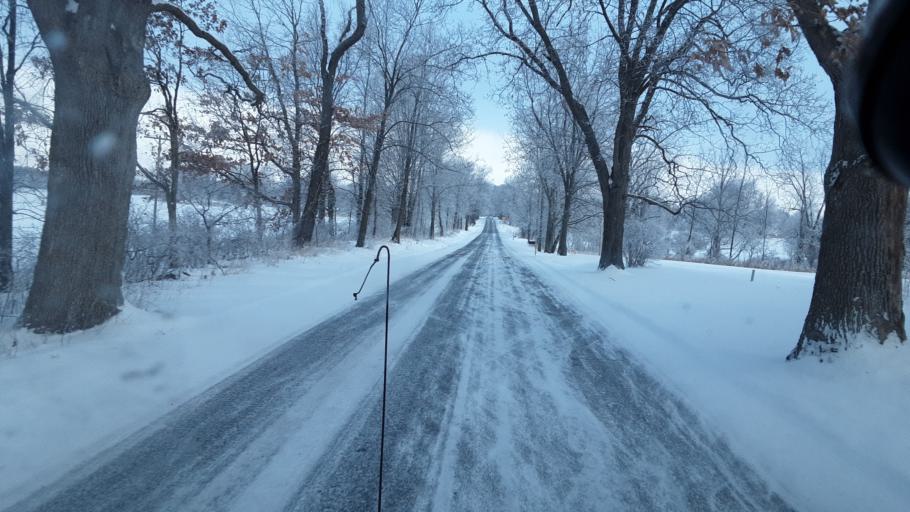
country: US
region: Michigan
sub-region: Ingham County
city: Leslie
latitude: 42.4319
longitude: -84.4970
